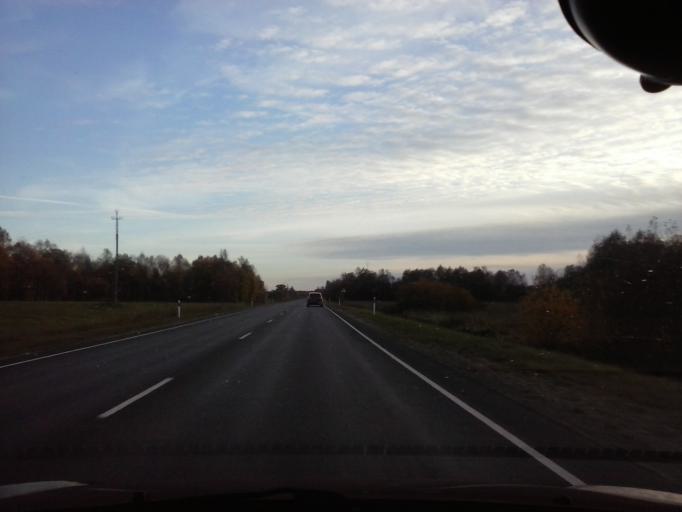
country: EE
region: Harju
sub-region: Nissi vald
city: Turba
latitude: 58.9160
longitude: 24.1121
